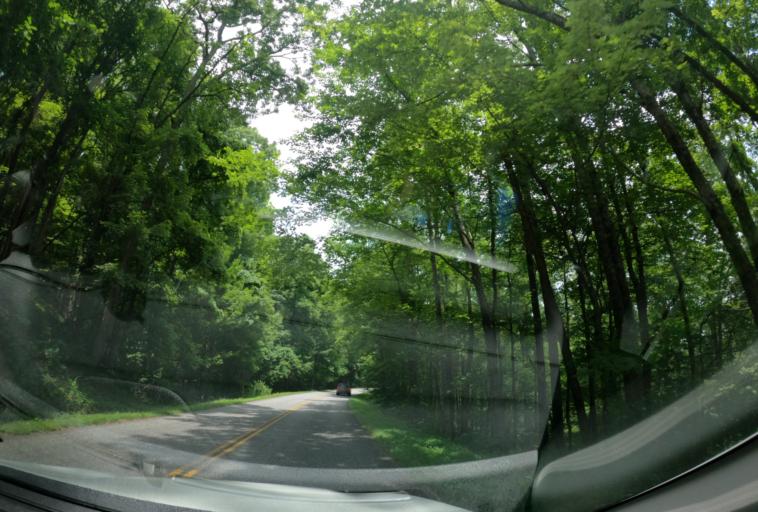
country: US
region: North Carolina
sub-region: Buncombe County
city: Avery Creek
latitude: 35.4675
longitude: -82.6258
